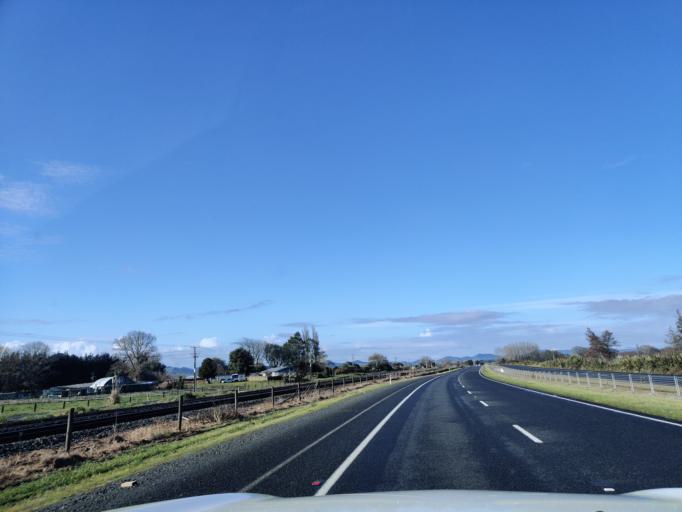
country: NZ
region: Waikato
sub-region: Waikato District
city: Te Kauwhata
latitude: -37.4760
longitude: 175.1595
